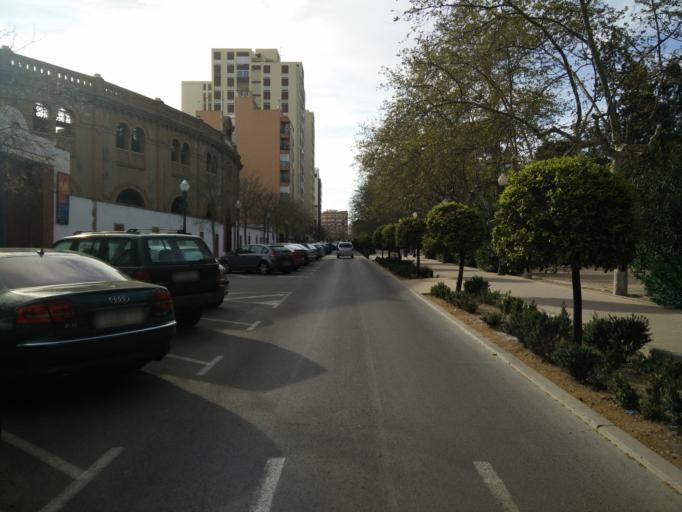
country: ES
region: Valencia
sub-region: Provincia de Castello
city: Castello de la Plana
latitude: 39.9861
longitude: -0.0445
